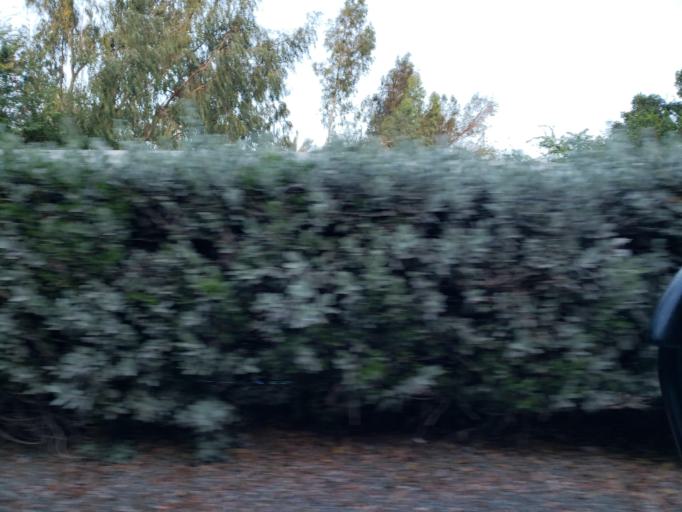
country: AE
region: Dubai
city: Dubai
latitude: 24.9856
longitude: 55.0226
